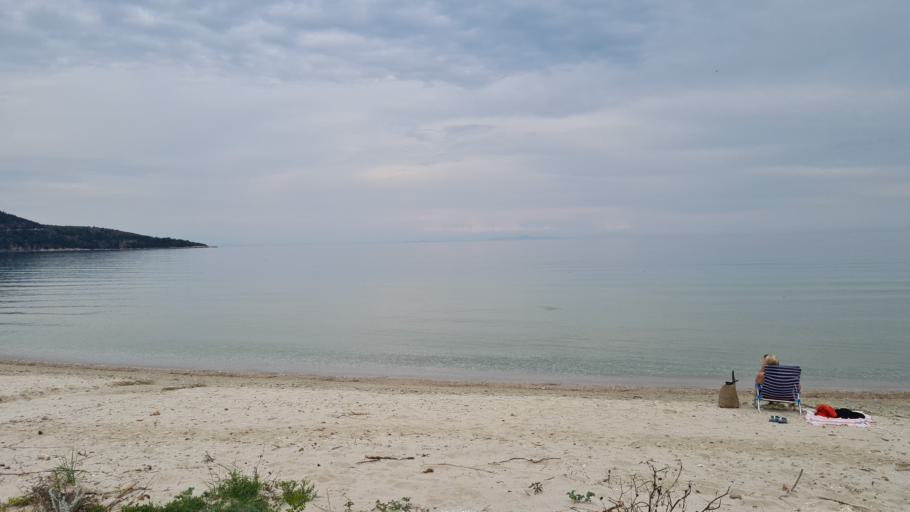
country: GR
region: East Macedonia and Thrace
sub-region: Nomos Kavalas
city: Potamia
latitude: 40.7135
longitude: 24.7579
